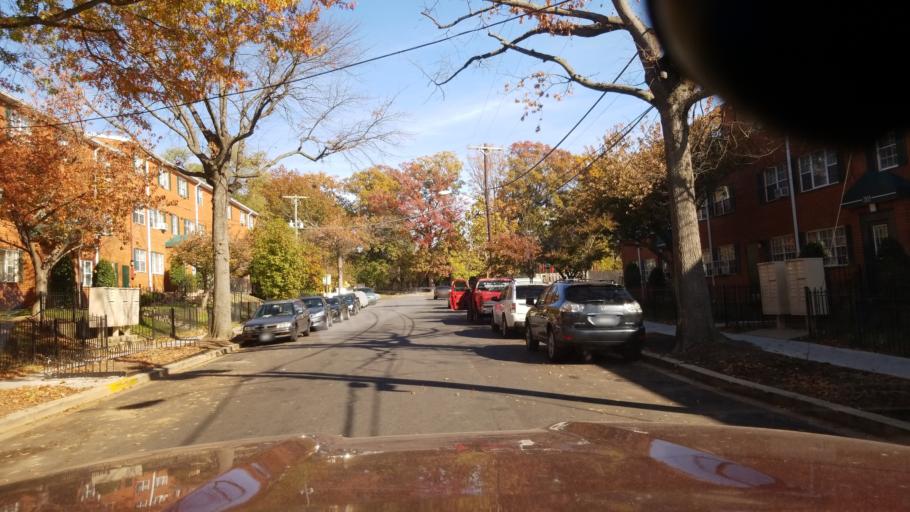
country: US
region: Maryland
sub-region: Prince George's County
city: Hillcrest Heights
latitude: 38.8483
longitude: -76.9731
